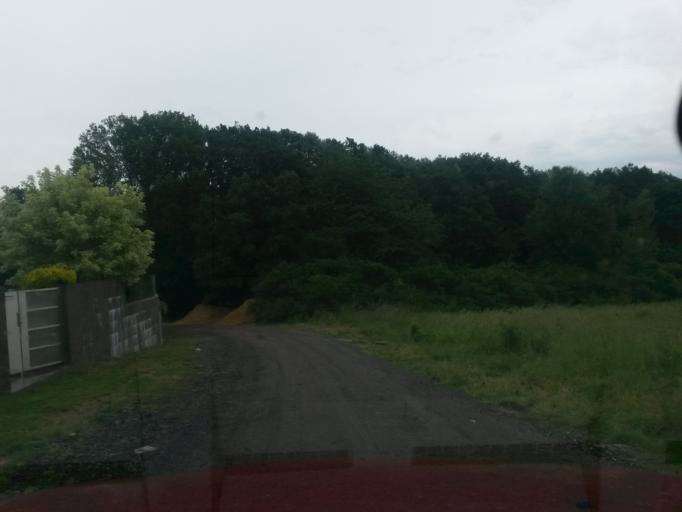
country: SK
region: Kosicky
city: Kosice
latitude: 48.7066
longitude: 21.1883
